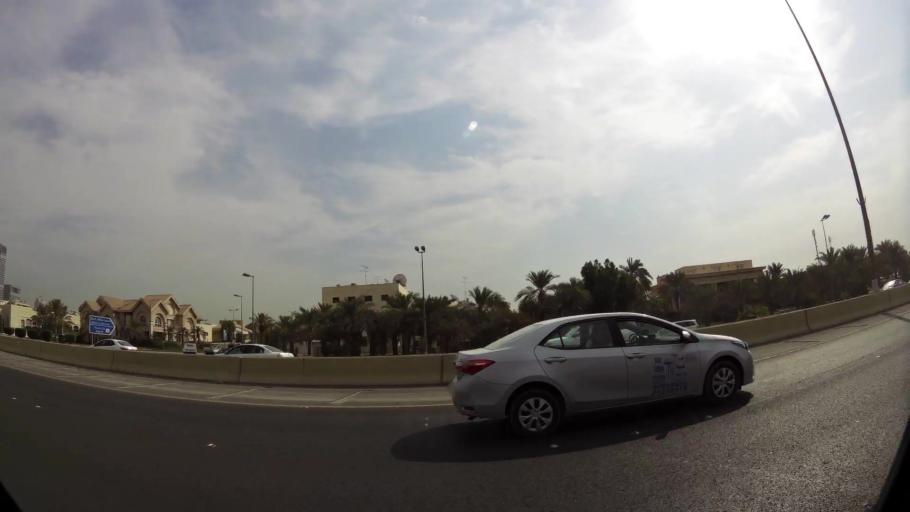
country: KW
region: Al Asimah
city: Ash Shamiyah
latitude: 29.3532
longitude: 47.9731
